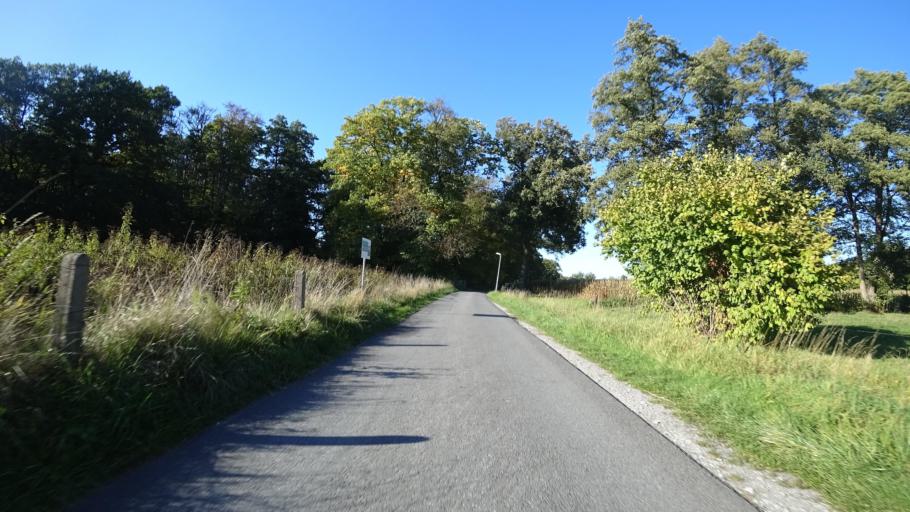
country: DE
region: North Rhine-Westphalia
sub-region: Regierungsbezirk Detmold
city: Guetersloh
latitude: 51.8762
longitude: 8.3598
